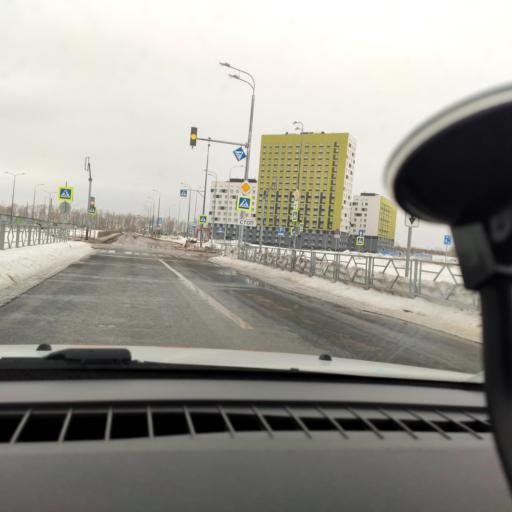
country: RU
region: Samara
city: Samara
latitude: 53.0993
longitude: 50.1739
